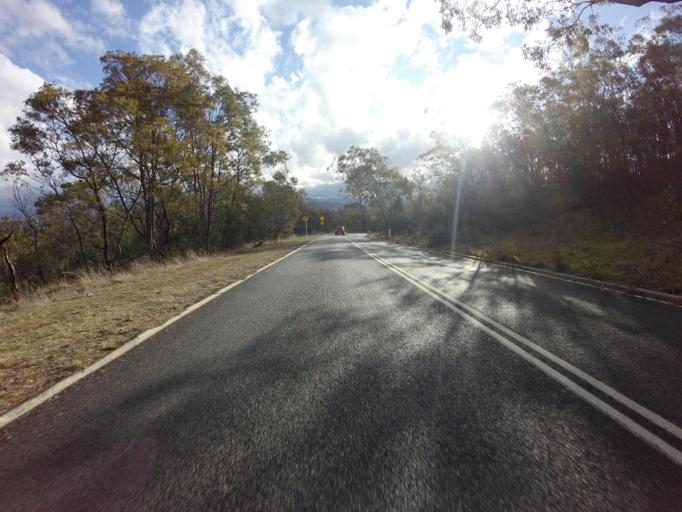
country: AU
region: Australian Capital Territory
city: Forrest
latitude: -35.3244
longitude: 149.1106
